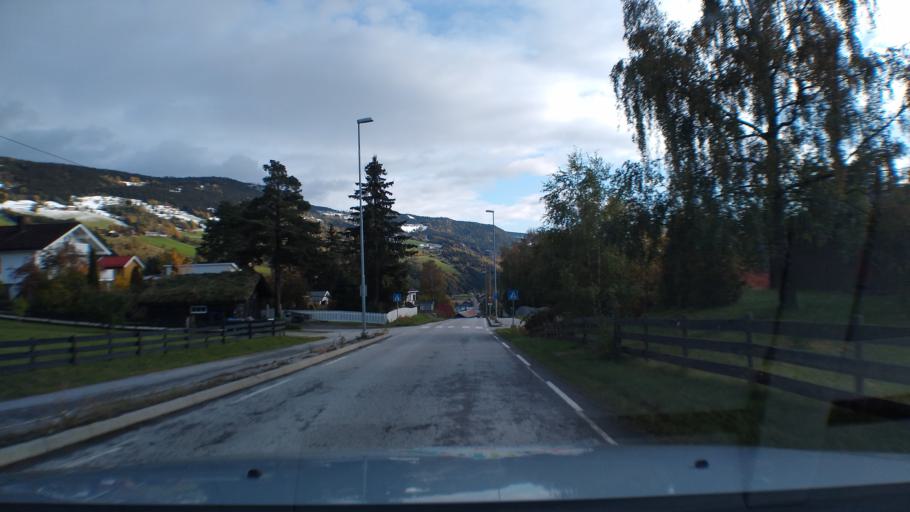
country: NO
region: Oppland
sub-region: Ringebu
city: Ringebu
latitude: 61.5348
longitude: 10.1356
